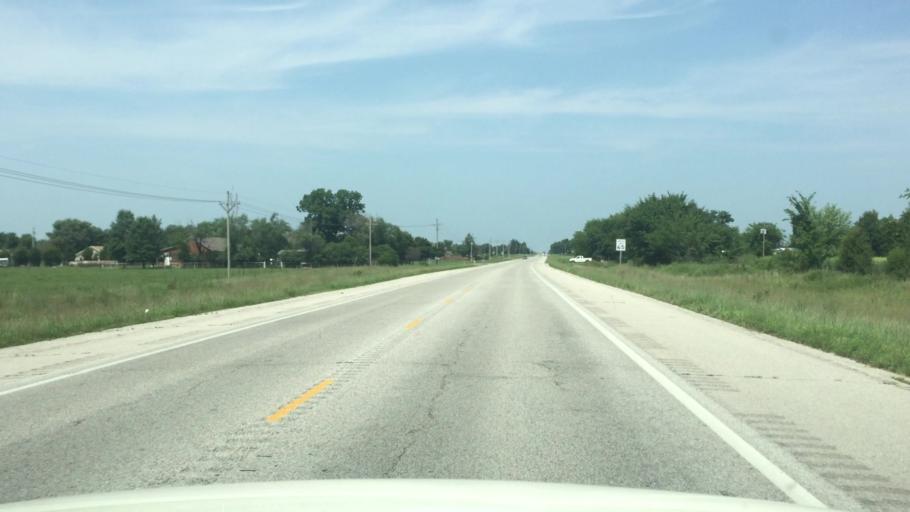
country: US
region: Kansas
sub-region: Cherokee County
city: Galena
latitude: 37.0913
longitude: -94.7044
